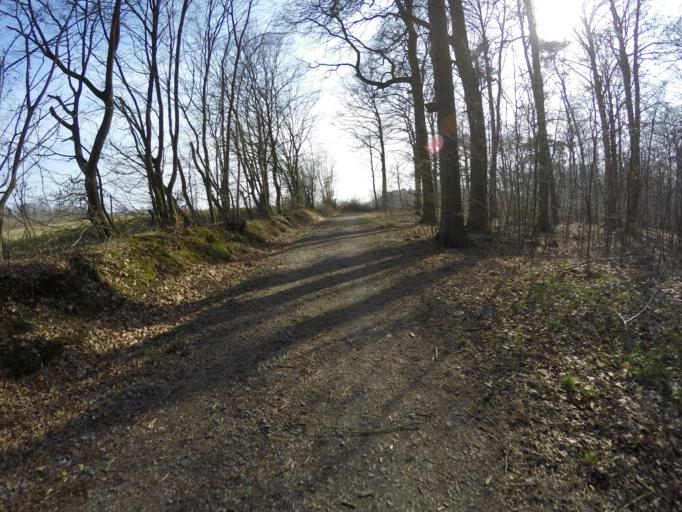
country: DE
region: Schleswig-Holstein
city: Borstel-Hohenraden
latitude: 53.7174
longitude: 9.8058
